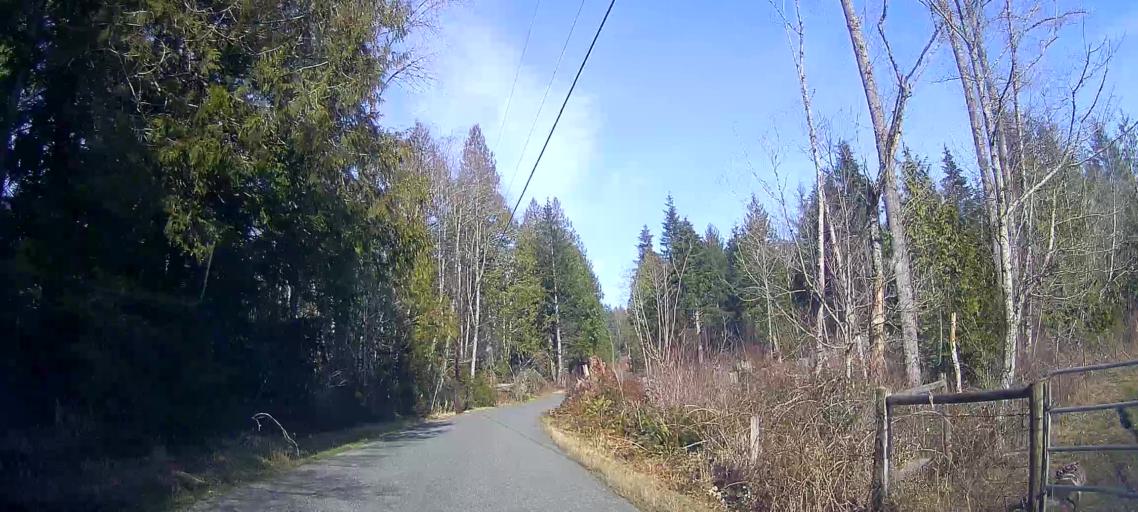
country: US
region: Washington
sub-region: Skagit County
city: Burlington
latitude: 48.5918
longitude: -122.3691
